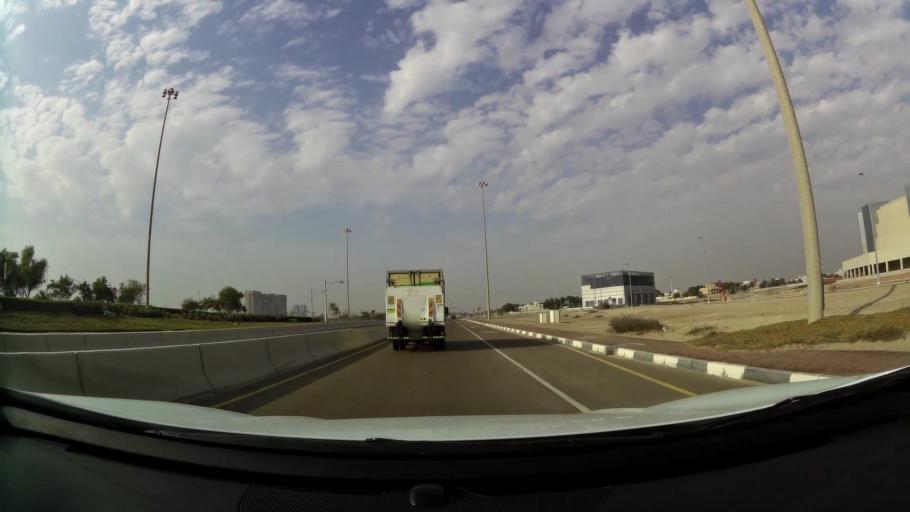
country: AE
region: Abu Dhabi
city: Abu Dhabi
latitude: 24.3756
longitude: 54.5275
